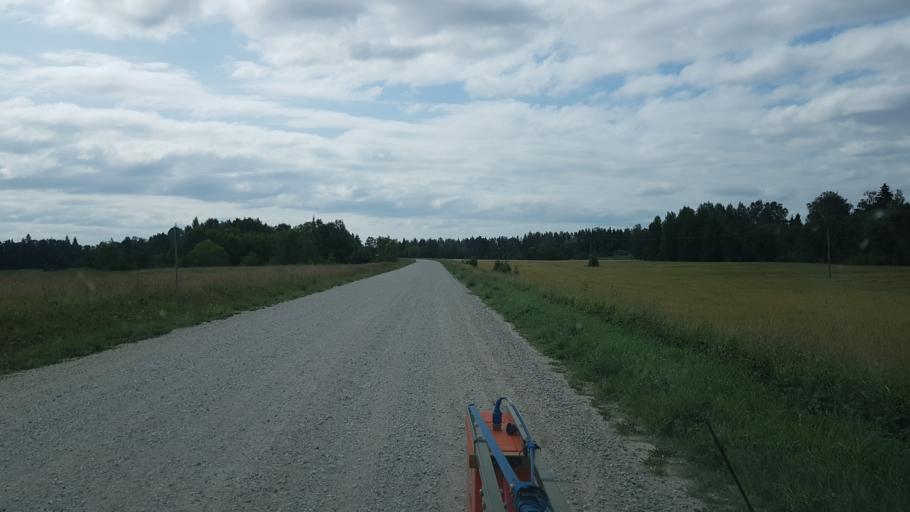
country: EE
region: Paernumaa
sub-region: Halinga vald
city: Parnu-Jaagupi
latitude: 58.5840
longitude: 24.4064
